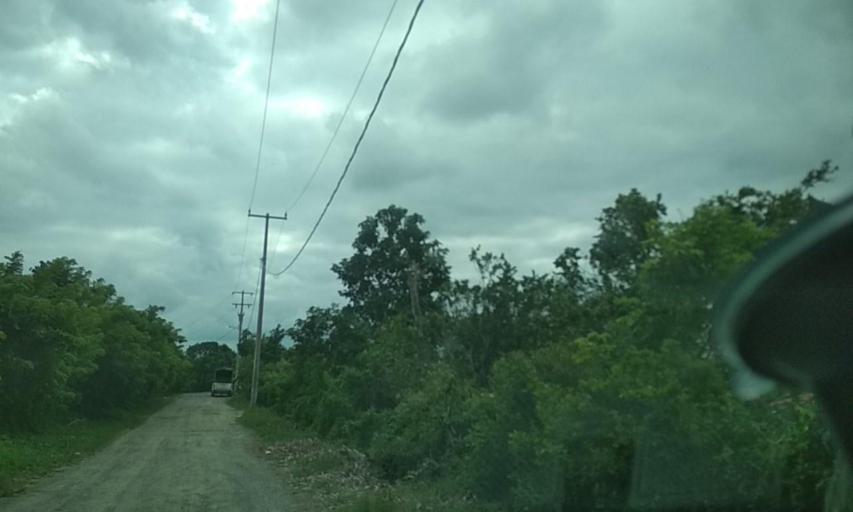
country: MX
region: Veracruz
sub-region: Papantla
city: Polutla
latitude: 20.5841
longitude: -97.2649
